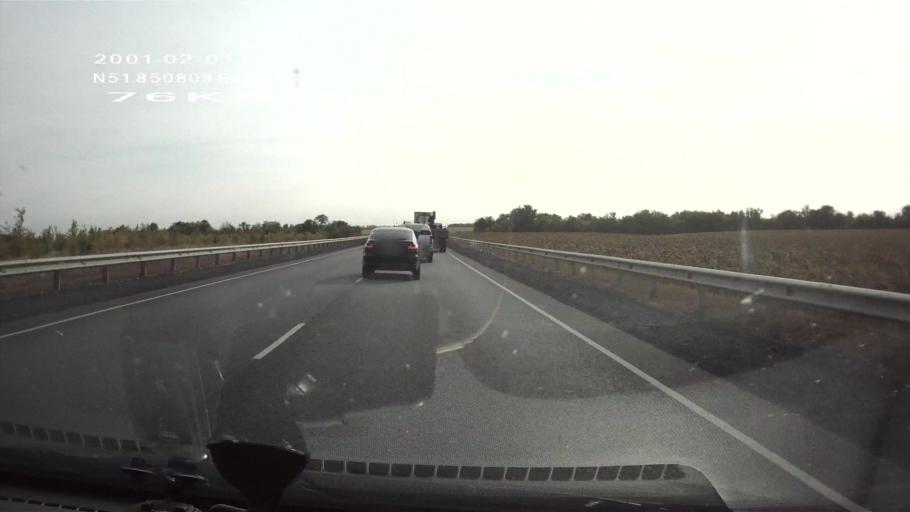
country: RU
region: Saratov
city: Yelshanka
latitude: 51.8507
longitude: 46.4885
